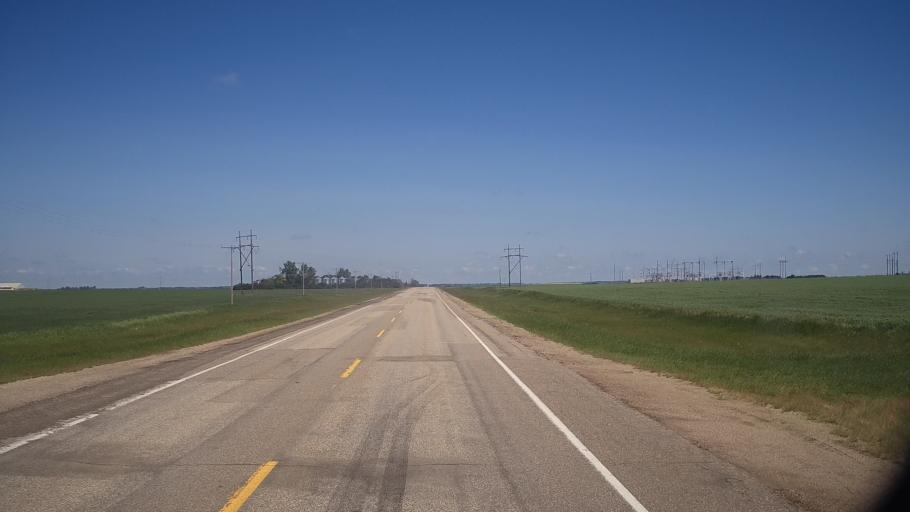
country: CA
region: Saskatchewan
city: Saskatoon
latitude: 51.9762
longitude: -106.0753
